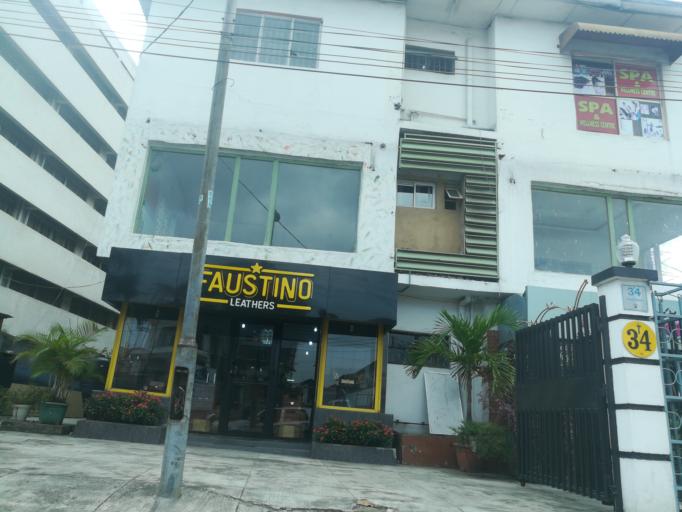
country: NG
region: Lagos
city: Ikeja
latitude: 6.5921
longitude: 3.3589
